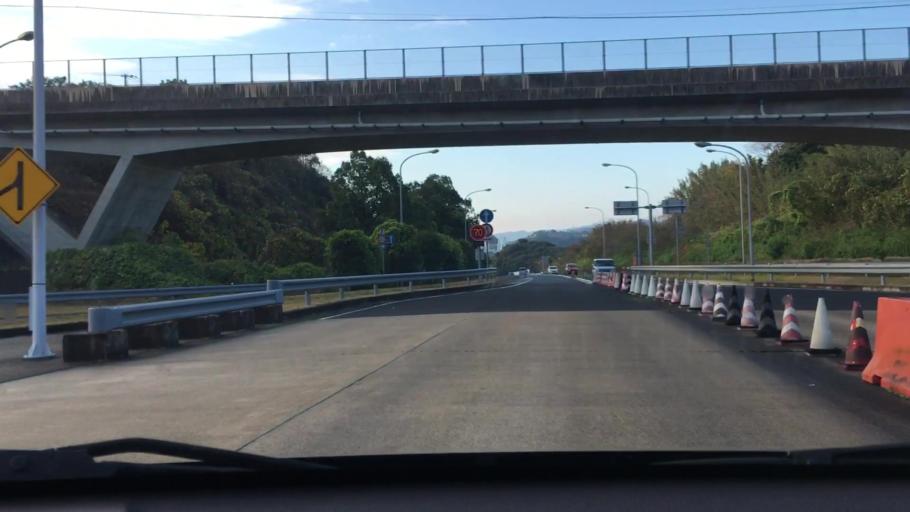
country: JP
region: Nagasaki
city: Sasebo
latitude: 33.0647
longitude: 129.7614
